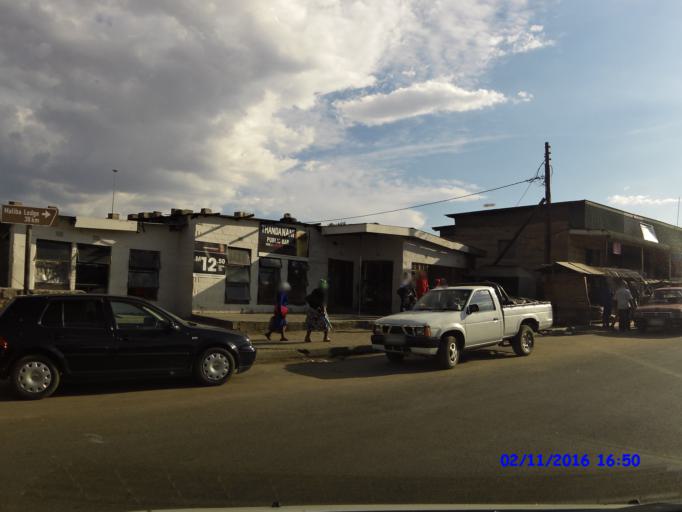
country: LS
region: Butha-Buthe
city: Butha-Buthe
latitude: -28.7676
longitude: 28.2523
